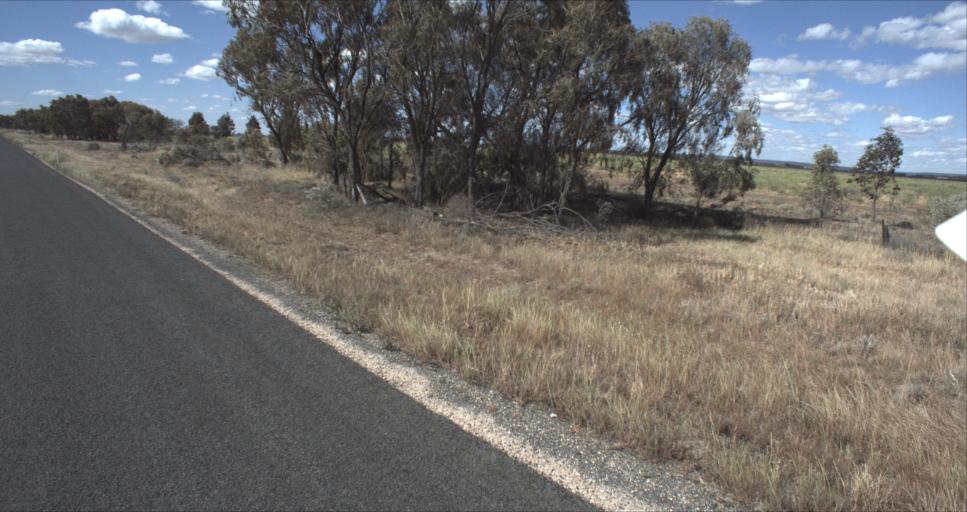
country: AU
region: New South Wales
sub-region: Leeton
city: Leeton
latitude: -34.4374
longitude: 146.2570
